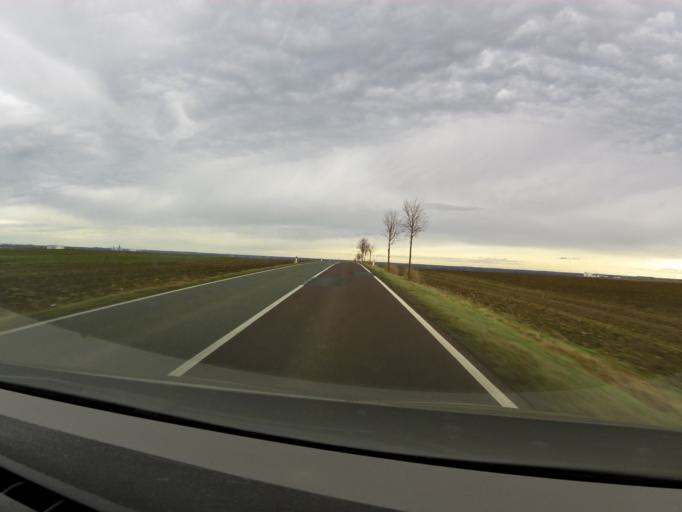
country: DE
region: Saxony-Anhalt
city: Alsleben
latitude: 51.6927
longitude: 11.6544
